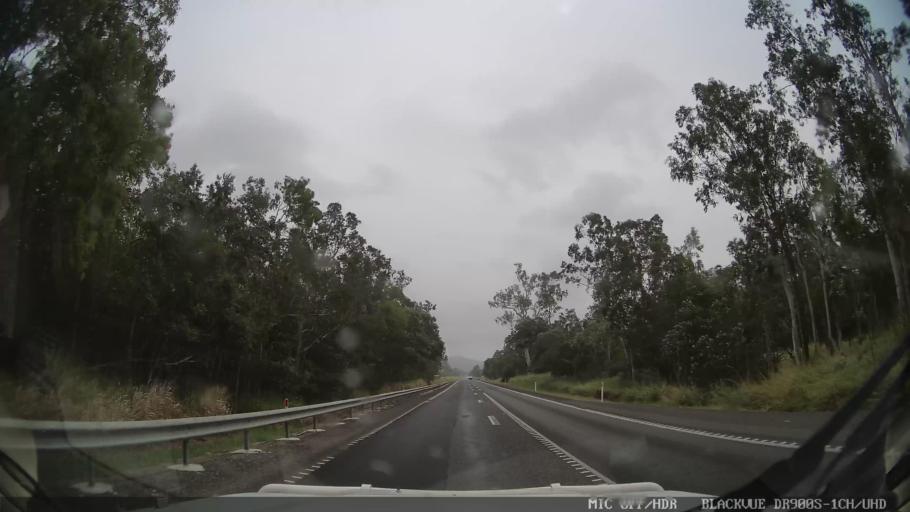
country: AU
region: Queensland
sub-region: Hinchinbrook
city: Ingham
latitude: -18.2110
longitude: 145.9645
